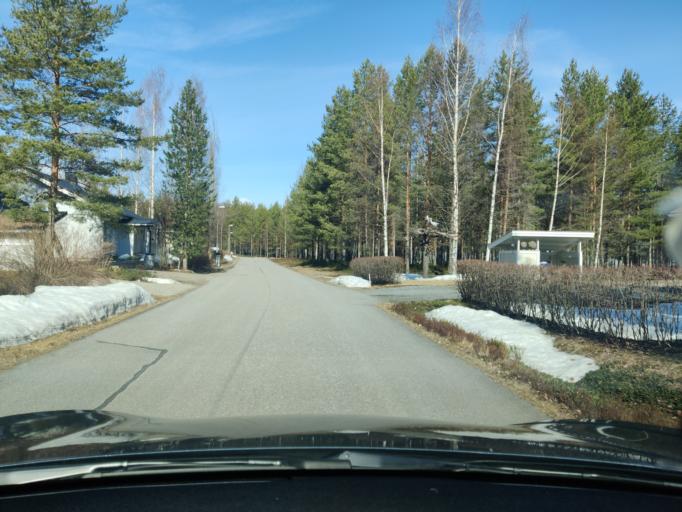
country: FI
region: Northern Savo
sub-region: Kuopio
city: Vehmersalmi
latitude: 62.7723
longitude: 27.9862
